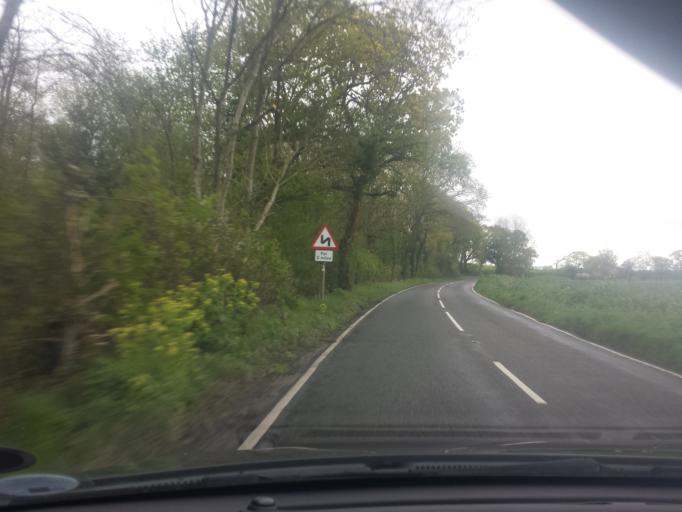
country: GB
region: England
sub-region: Suffolk
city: Shotley Gate
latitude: 51.9330
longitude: 1.1774
